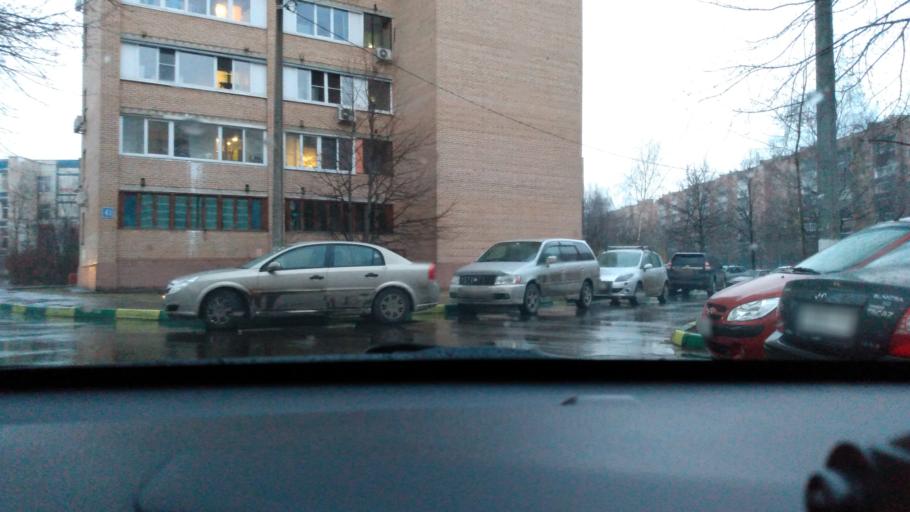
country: RU
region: Moskovskaya
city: Lyubertsy
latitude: 55.6754
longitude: 37.8702
